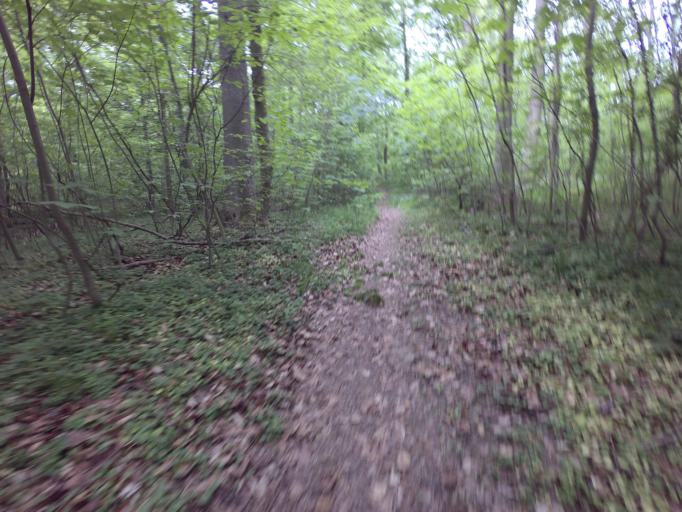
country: DE
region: Lower Saxony
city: Diekholzen
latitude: 52.1147
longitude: 9.9080
